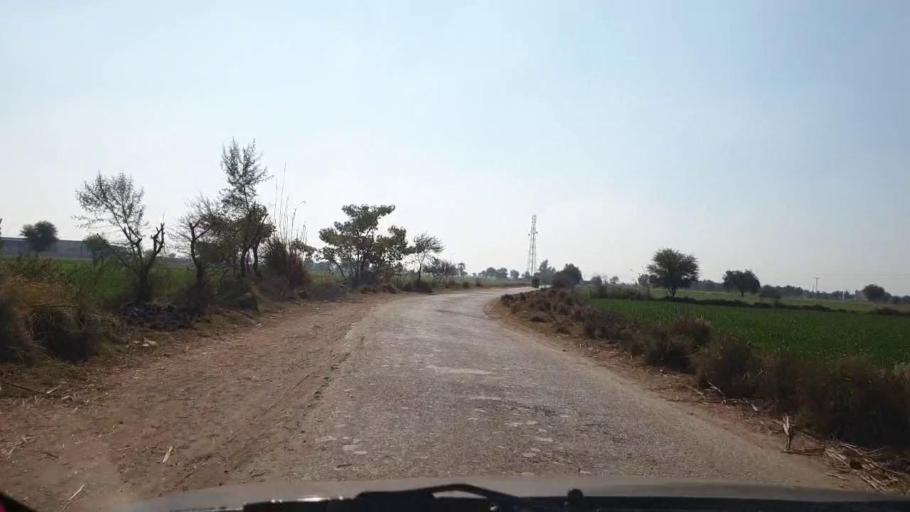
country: PK
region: Sindh
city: Sinjhoro
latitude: 25.9419
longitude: 68.7469
